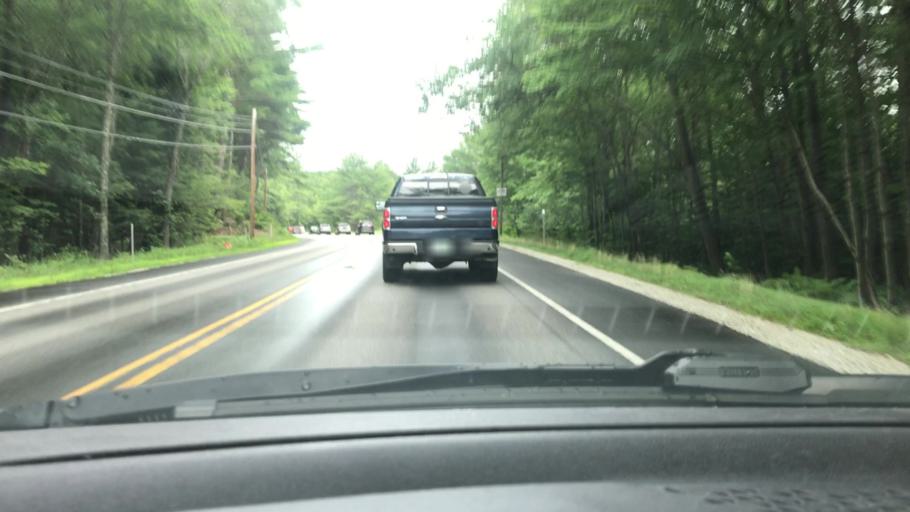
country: US
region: New Hampshire
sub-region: Merrimack County
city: Epsom
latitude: 43.2244
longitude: -71.3069
